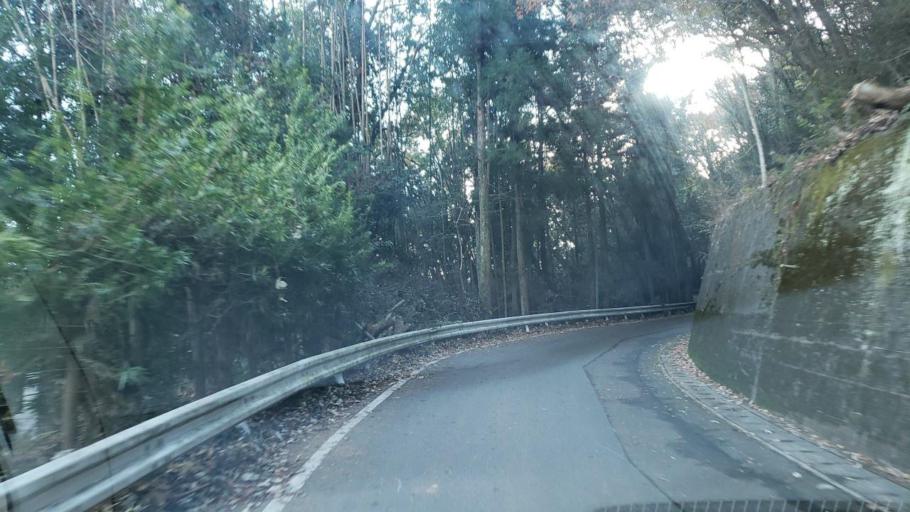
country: JP
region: Tokushima
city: Wakimachi
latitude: 34.1119
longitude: 134.0782
